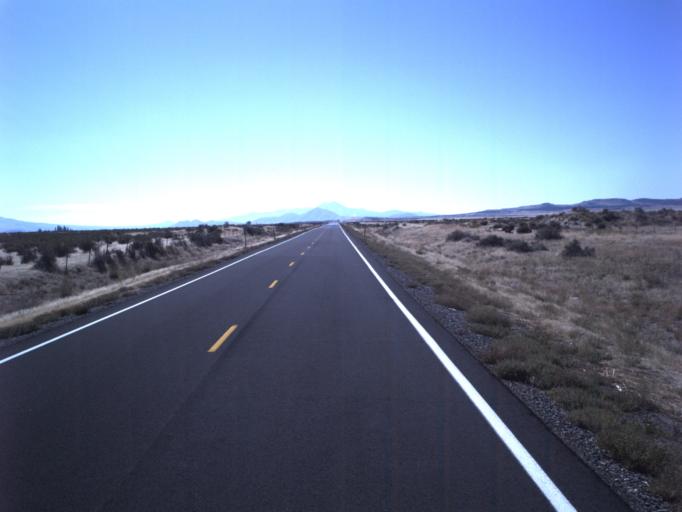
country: US
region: Utah
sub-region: Tooele County
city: Grantsville
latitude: 40.3275
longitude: -112.7442
